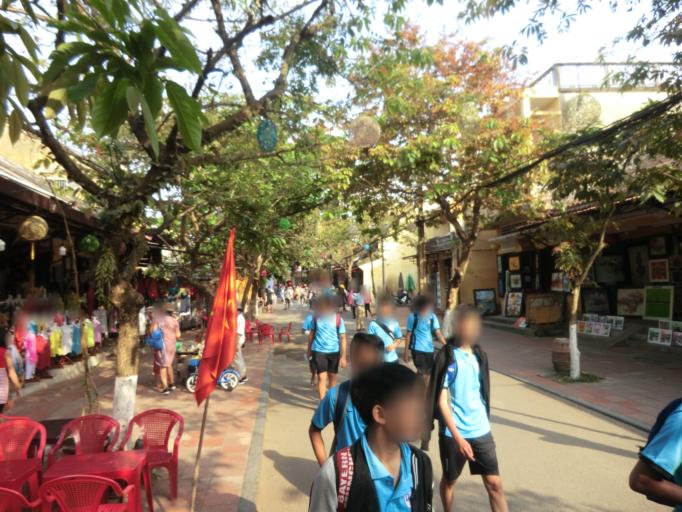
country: VN
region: Quang Nam
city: Hoi An
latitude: 15.8774
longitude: 108.3250
